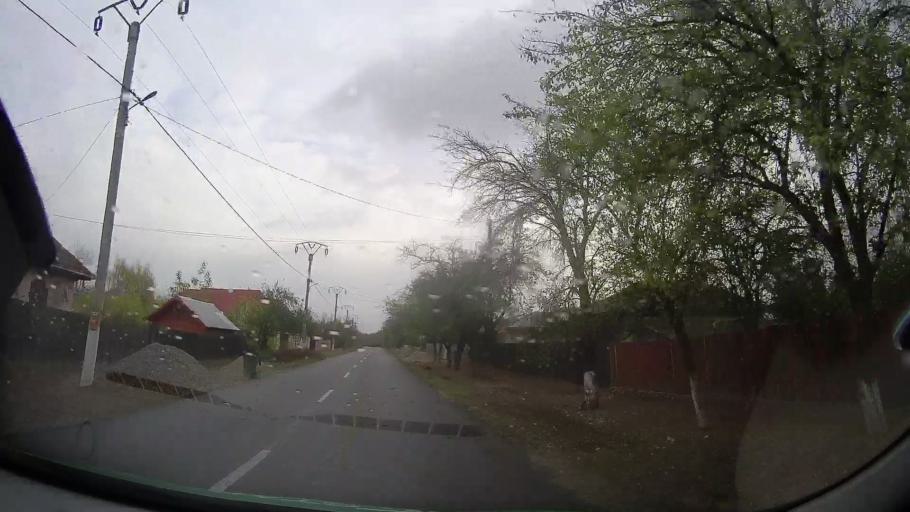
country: RO
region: Ialomita
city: Brazii
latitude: 44.7799
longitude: 26.3329
